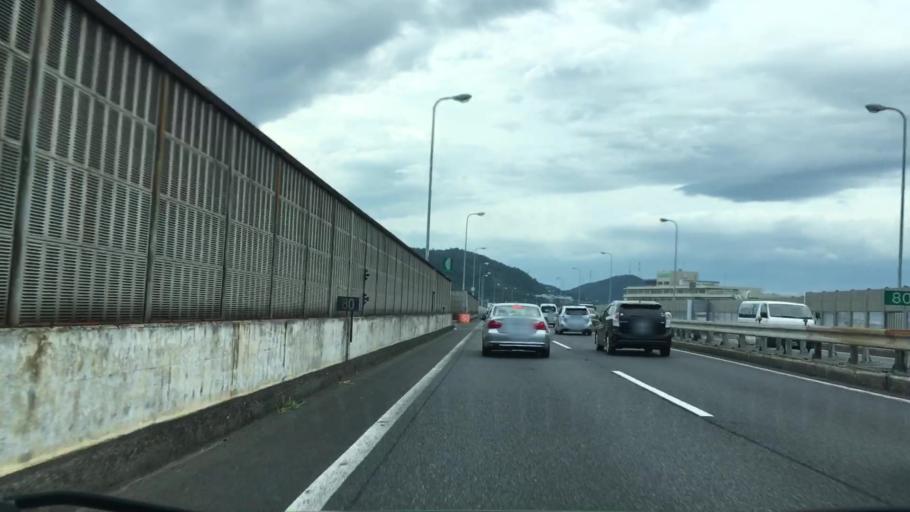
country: JP
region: Hyogo
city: Kakogawacho-honmachi
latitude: 34.7872
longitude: 134.7756
